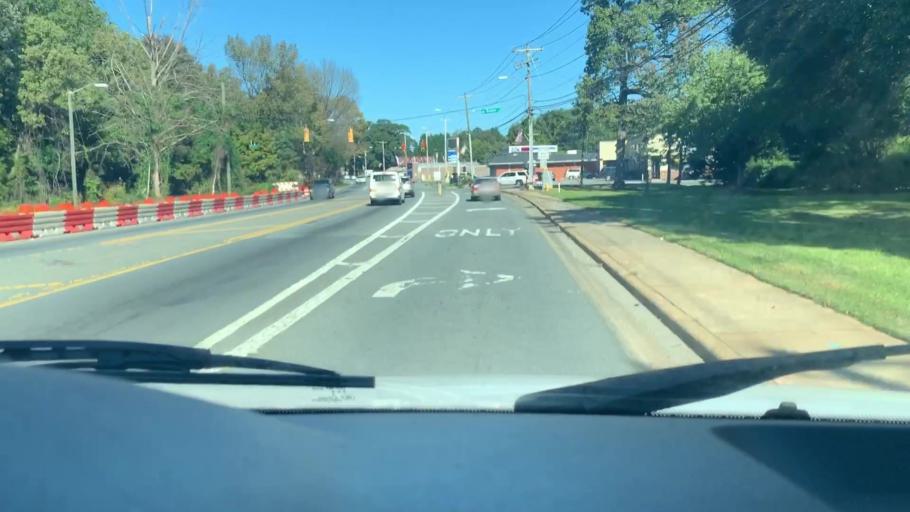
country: US
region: North Carolina
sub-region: Mecklenburg County
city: Charlotte
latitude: 35.2949
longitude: -80.7976
